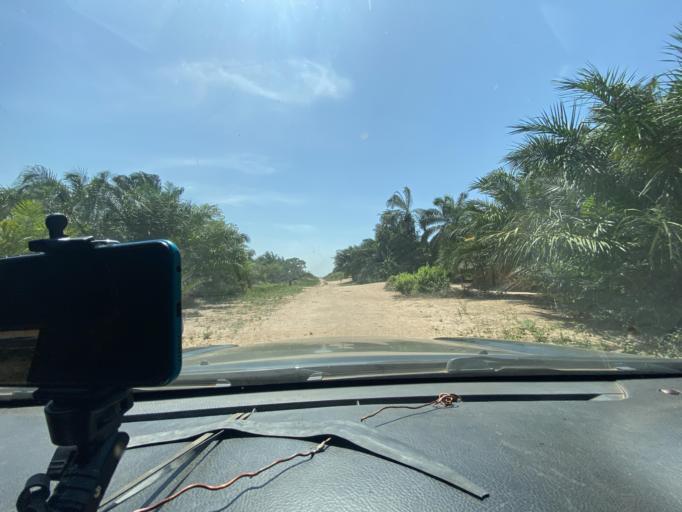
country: CD
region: Kasai-Oriental
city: Kabinda
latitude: -5.9518
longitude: 24.8043
